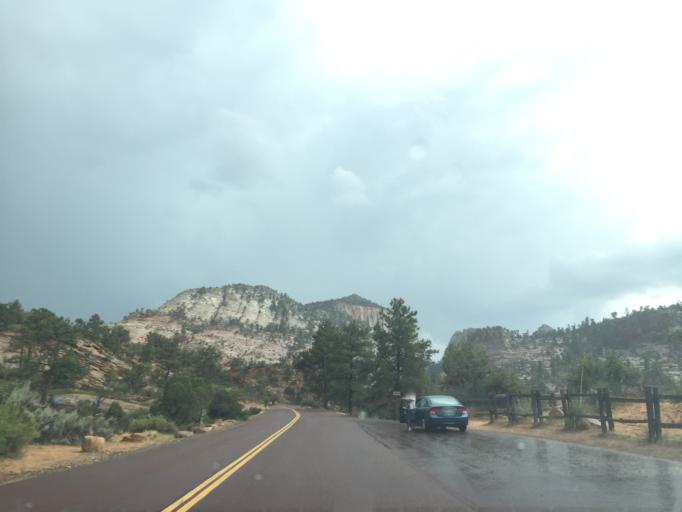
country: US
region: Utah
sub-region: Washington County
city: Hildale
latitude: 37.2250
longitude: -112.9093
